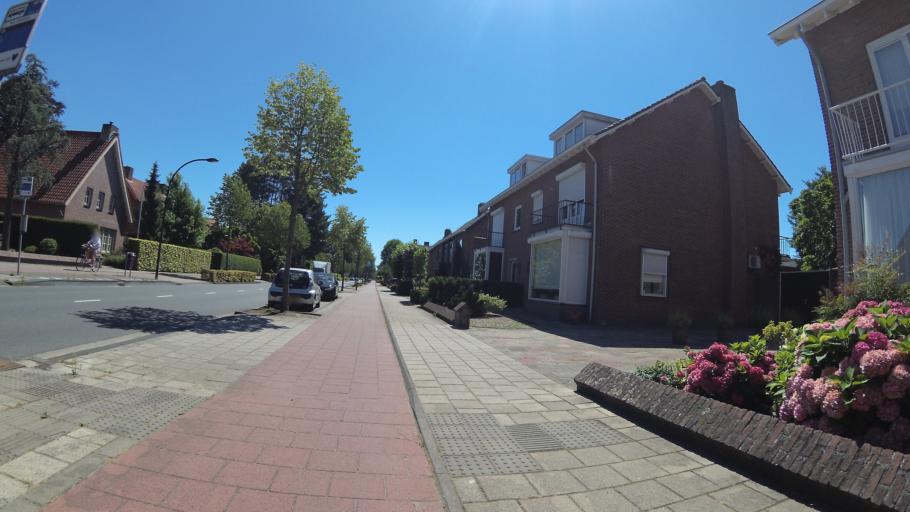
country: NL
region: North Brabant
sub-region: Gemeente Waalwijk
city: Waalwijk
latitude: 51.6833
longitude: 5.0763
